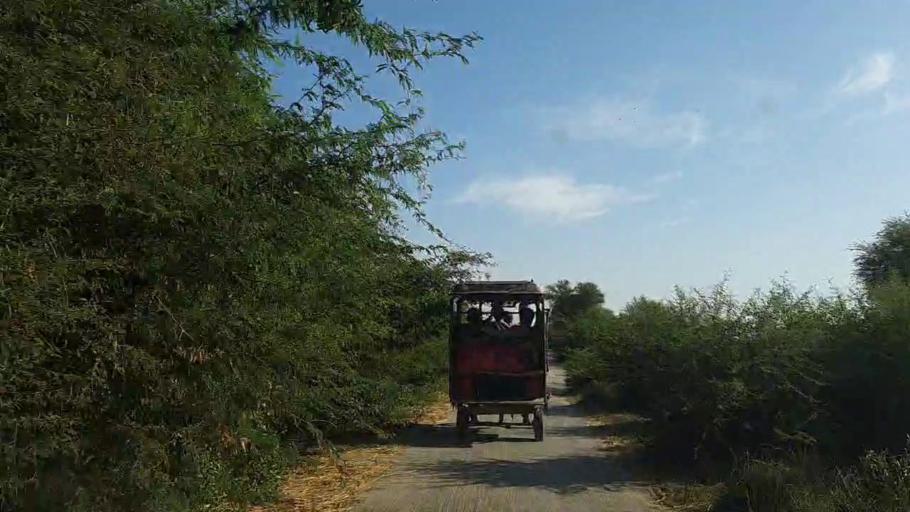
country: PK
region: Sindh
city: Bulri
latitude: 24.7975
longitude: 68.3389
